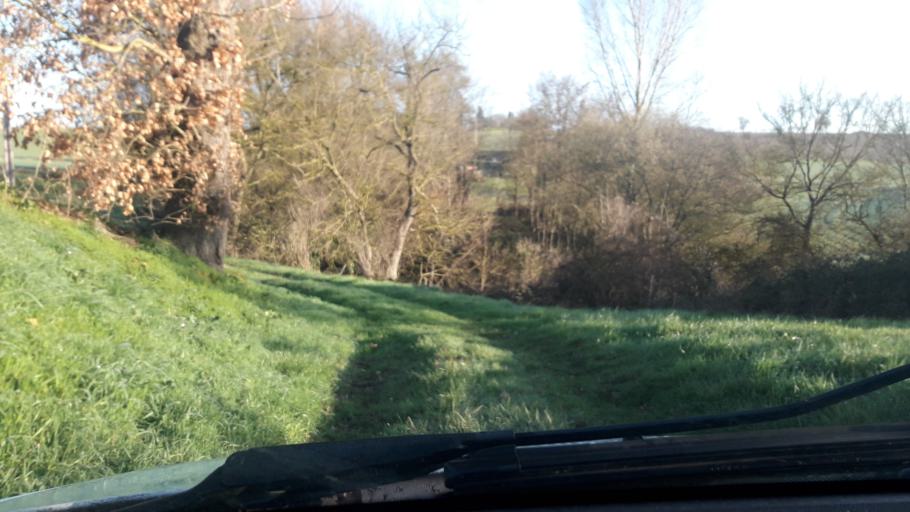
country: FR
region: Midi-Pyrenees
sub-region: Departement du Gers
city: Gimont
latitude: 43.6358
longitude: 0.9962
